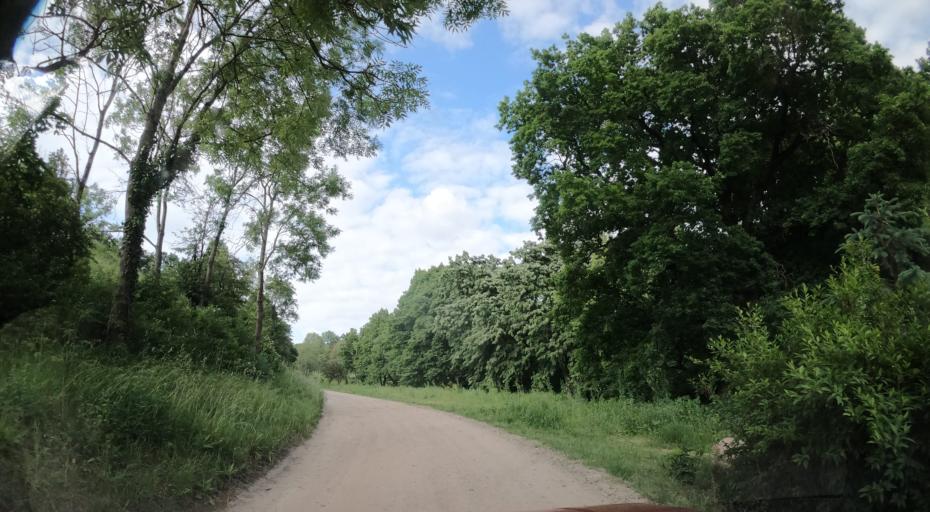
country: PL
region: Lubusz
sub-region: Powiat gorzowski
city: Santok
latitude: 52.7362
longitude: 15.3972
